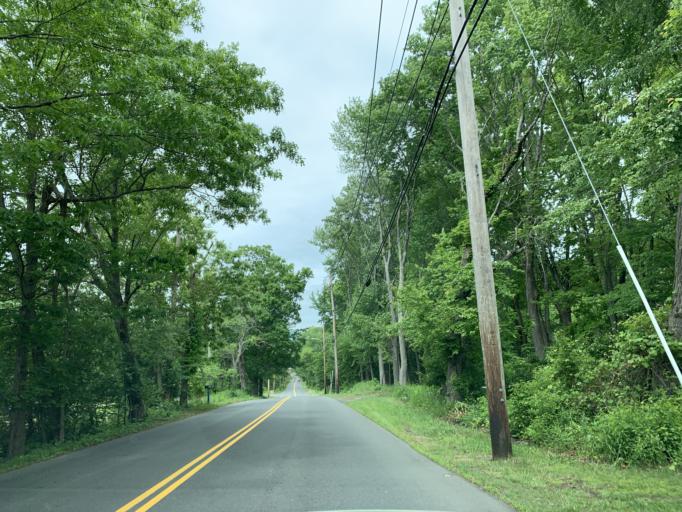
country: US
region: Massachusetts
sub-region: Hampshire County
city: Southampton
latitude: 42.1857
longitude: -72.7431
